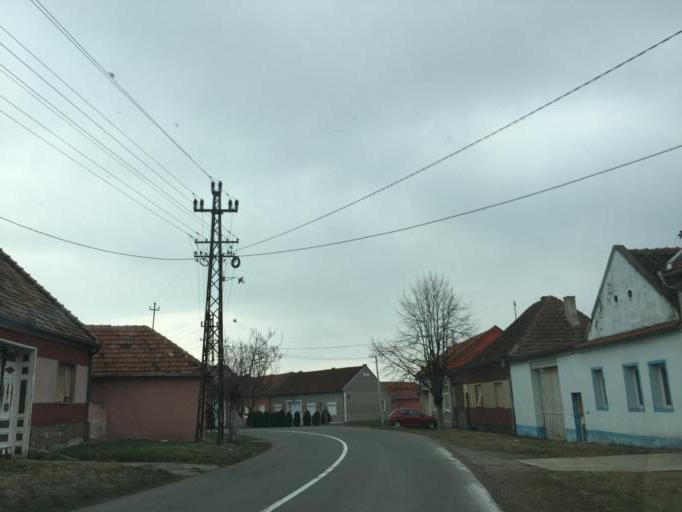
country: RS
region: Central Serbia
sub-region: Branicevski Okrug
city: Pozarevac
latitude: 44.7947
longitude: 21.1997
